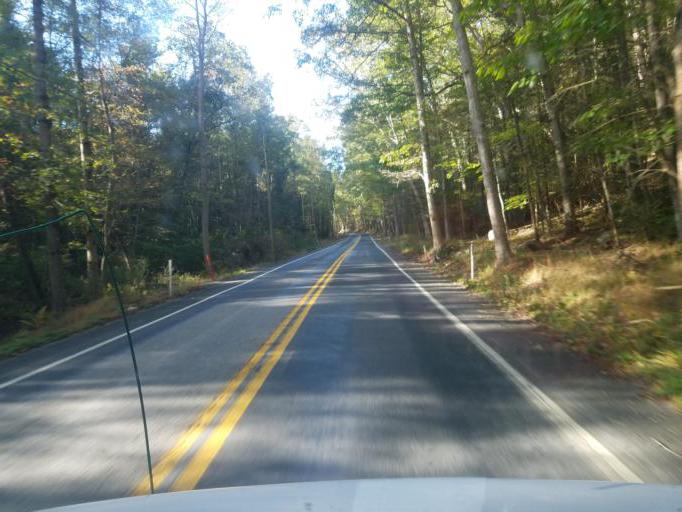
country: US
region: Pennsylvania
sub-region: Franklin County
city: Fayetteville
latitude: 39.8975
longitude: -77.4823
